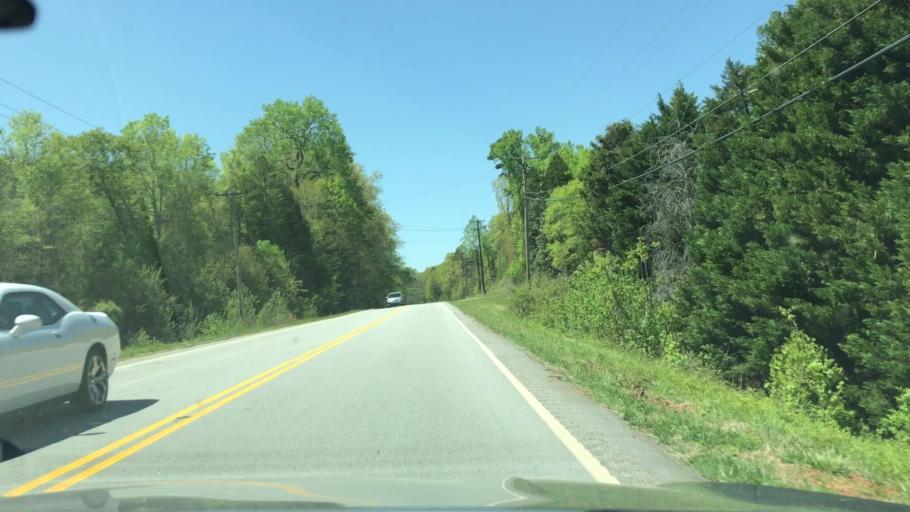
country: US
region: South Carolina
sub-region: Union County
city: Buffalo
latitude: 34.6813
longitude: -81.6968
